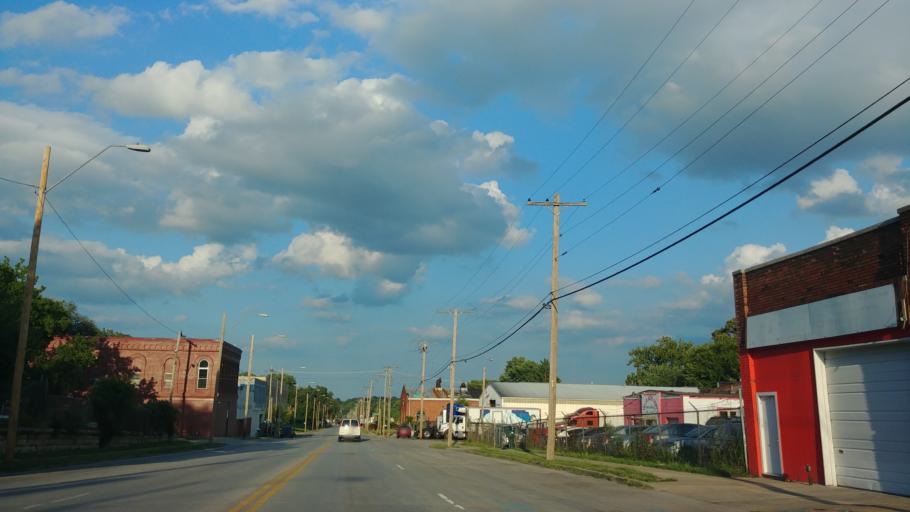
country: US
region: Missouri
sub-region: Clay County
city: North Kansas City
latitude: 39.0985
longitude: -94.5398
